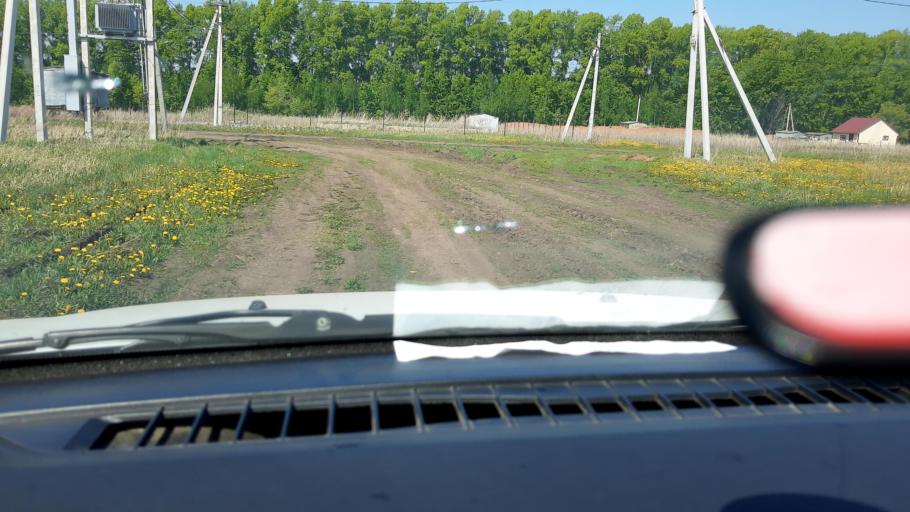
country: RU
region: Bashkortostan
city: Kabakovo
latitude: 54.6978
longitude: 56.1749
